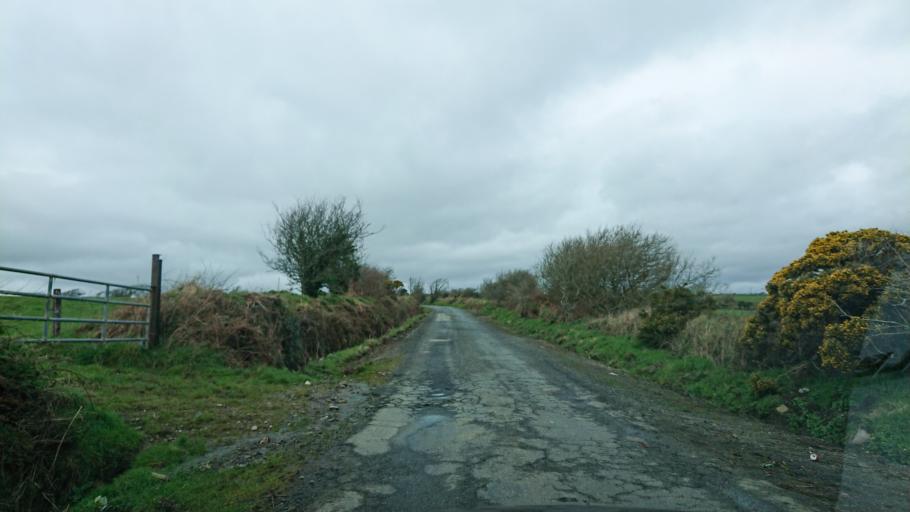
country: IE
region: Munster
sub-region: Waterford
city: Dunmore East
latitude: 52.1701
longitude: -7.0427
